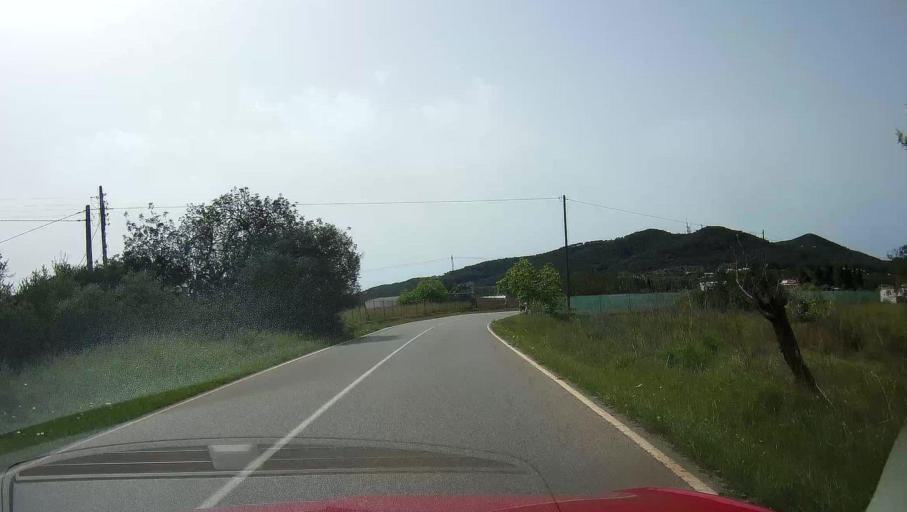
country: ES
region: Balearic Islands
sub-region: Illes Balears
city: Santa Eularia des Riu
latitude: 38.9856
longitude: 1.4933
